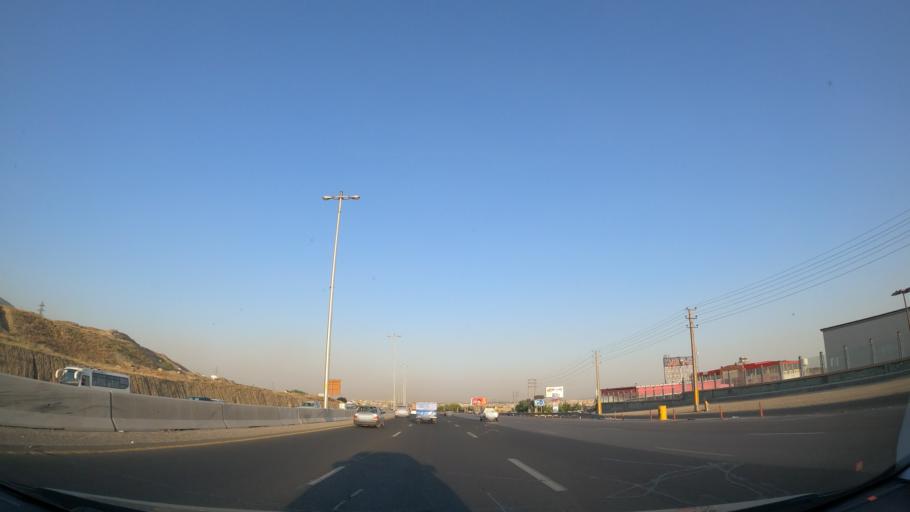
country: IR
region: Tehran
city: Shahr-e Qods
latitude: 35.7471
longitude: 51.0861
